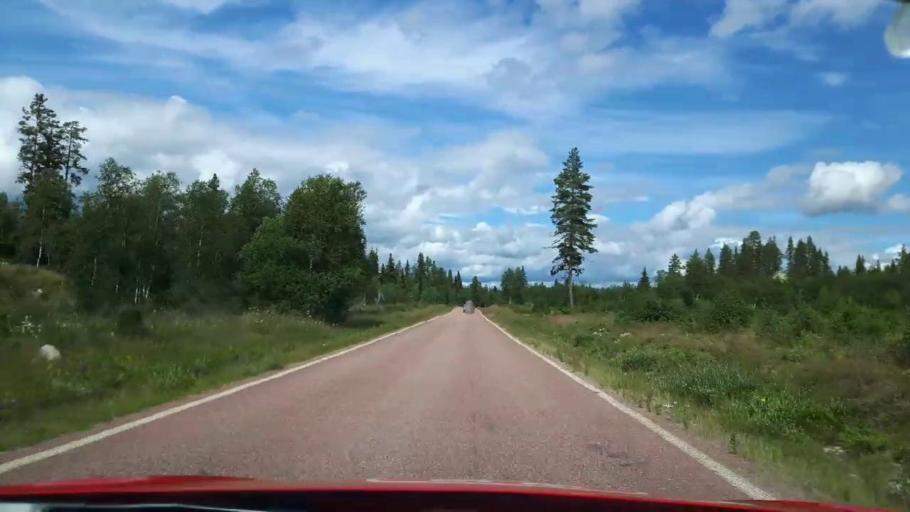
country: NO
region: Hedmark
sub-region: Trysil
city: Innbygda
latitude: 62.0048
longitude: 12.9762
